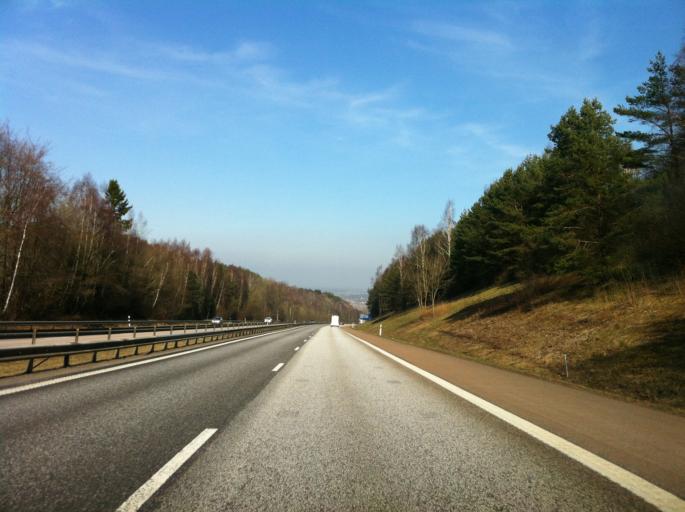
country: SE
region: Skane
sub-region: Bastads Kommun
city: Bastad
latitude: 56.4051
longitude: 12.9441
